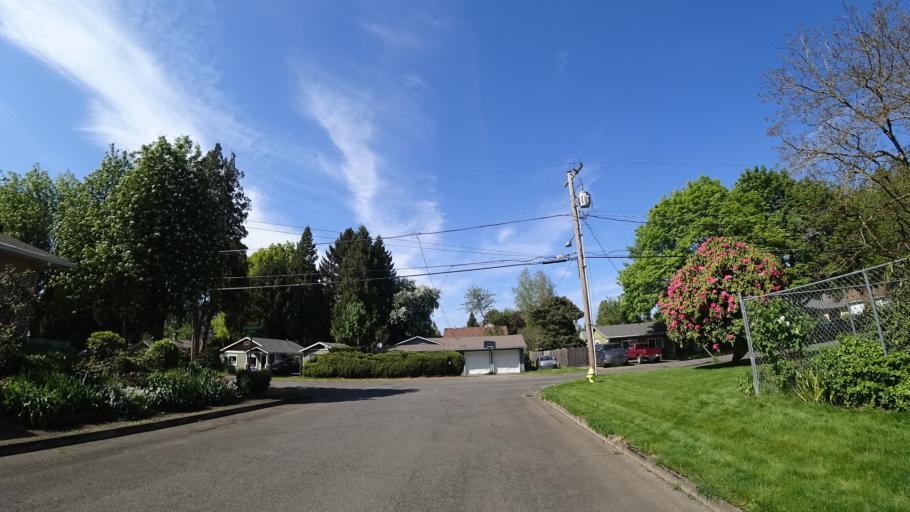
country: US
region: Oregon
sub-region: Clackamas County
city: Milwaukie
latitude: 45.4536
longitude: -122.6276
